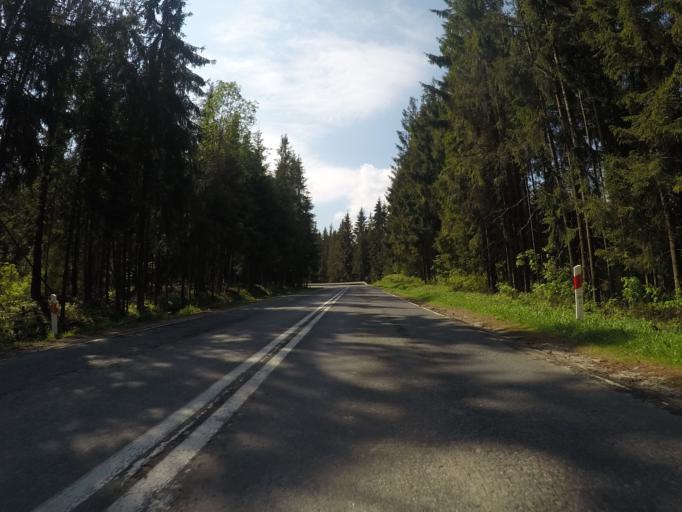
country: PL
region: Lesser Poland Voivodeship
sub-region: Powiat tatrzanski
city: Bukowina Tatrzanska
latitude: 49.3121
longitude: 20.1091
